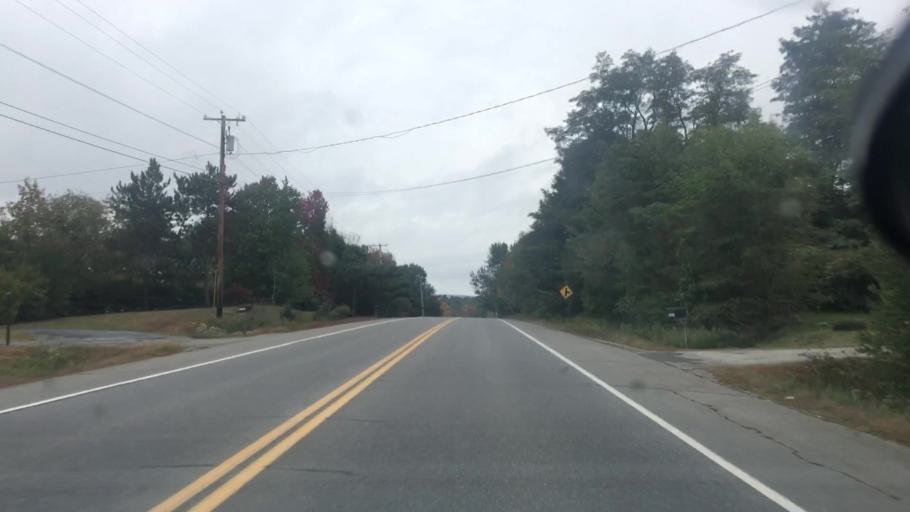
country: US
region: Maine
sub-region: Kennebec County
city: Belgrade
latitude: 44.3915
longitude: -69.8027
